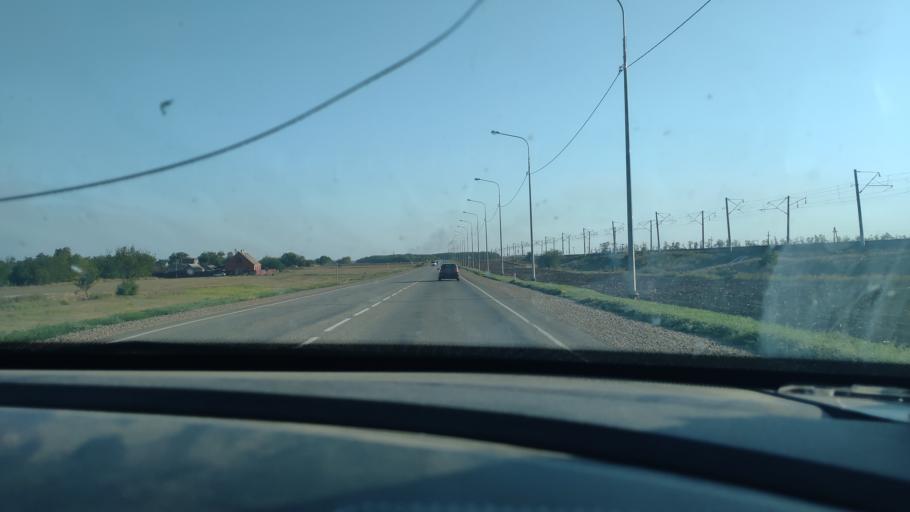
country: RU
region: Krasnodarskiy
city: Novominskaya
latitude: 46.3149
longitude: 38.9306
